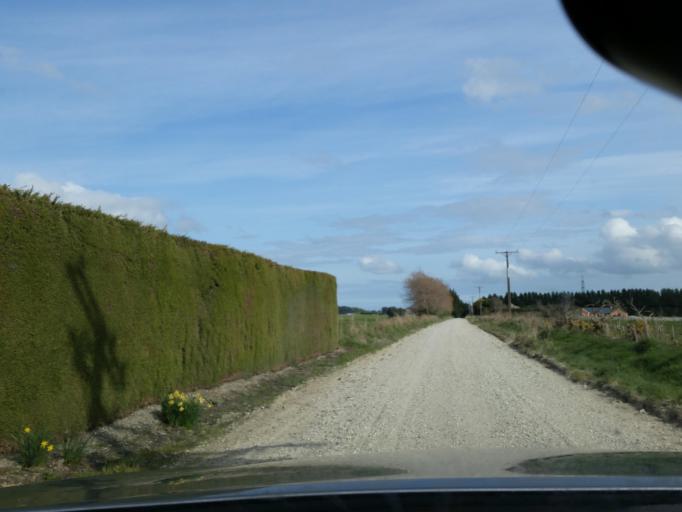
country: NZ
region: Southland
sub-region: Invercargill City
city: Invercargill
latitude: -46.2950
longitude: 168.4793
